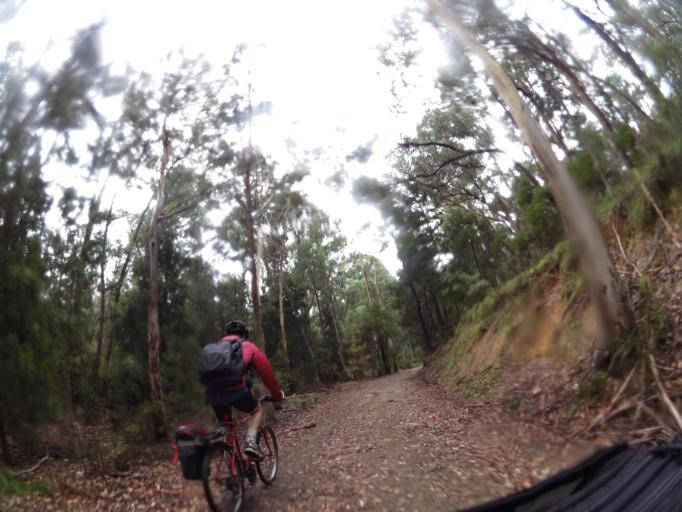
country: AU
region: New South Wales
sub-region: Greater Hume Shire
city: Holbrook
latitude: -36.1980
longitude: 147.5220
